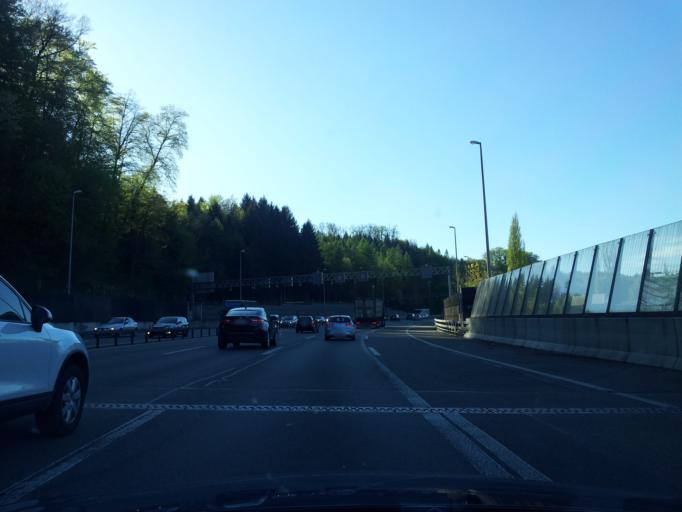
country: CH
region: Aargau
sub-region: Bezirk Baden
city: Neuenhof
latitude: 47.4534
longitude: 8.3110
